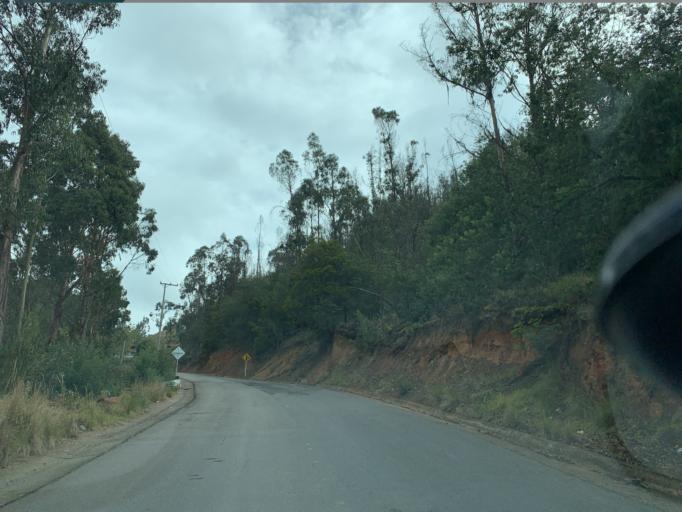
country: CO
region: Boyaca
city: Tunja
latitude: 5.5589
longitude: -73.3631
